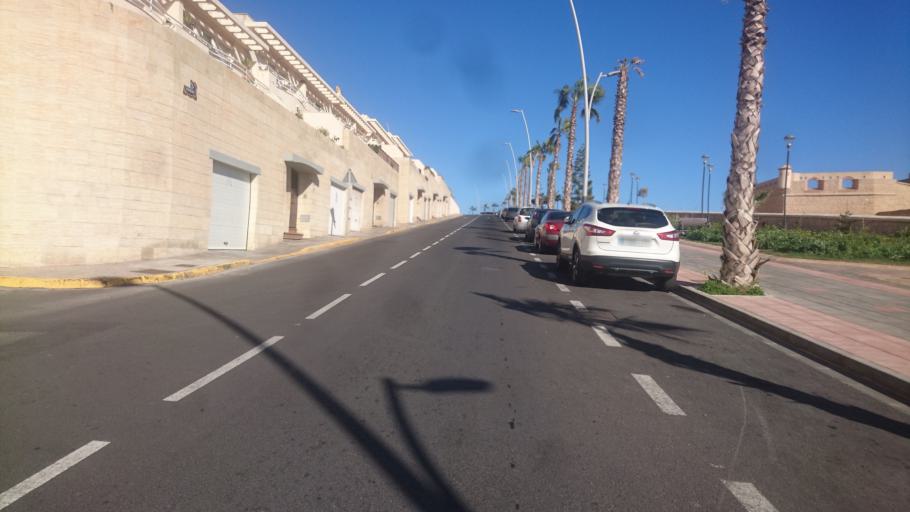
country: ES
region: Melilla
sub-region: Melilla
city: Melilla
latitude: 35.2945
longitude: -2.9367
